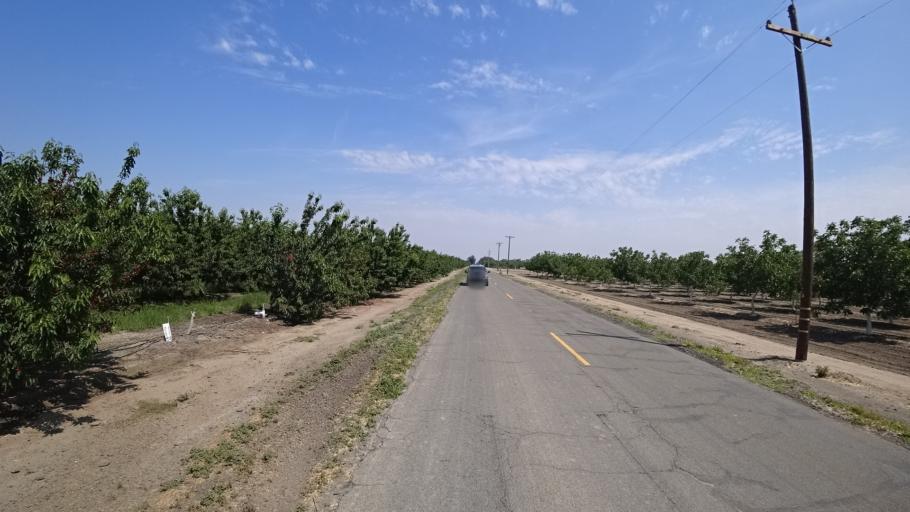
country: US
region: California
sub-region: Kings County
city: Armona
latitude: 36.3525
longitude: -119.7449
